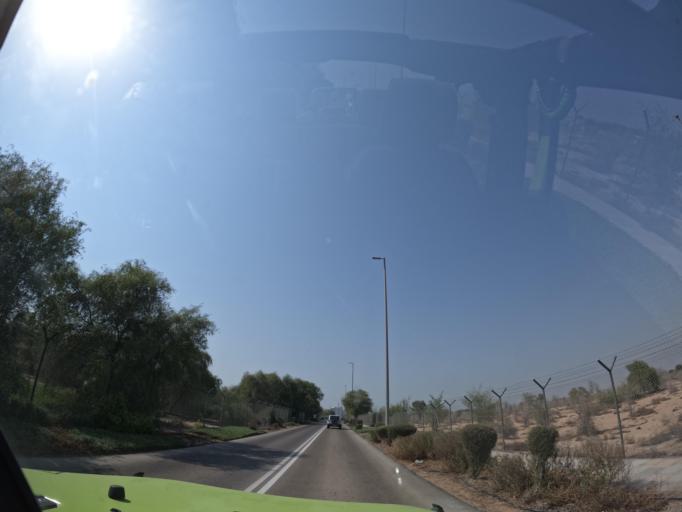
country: AE
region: Abu Dhabi
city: Abu Dhabi
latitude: 24.4740
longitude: 54.6293
